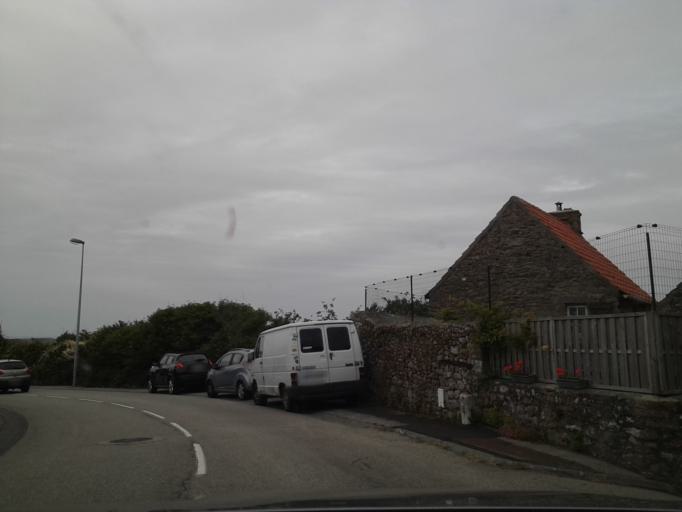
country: FR
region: Lower Normandy
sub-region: Departement de la Manche
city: Beaumont-Hague
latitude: 49.7133
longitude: -1.9306
